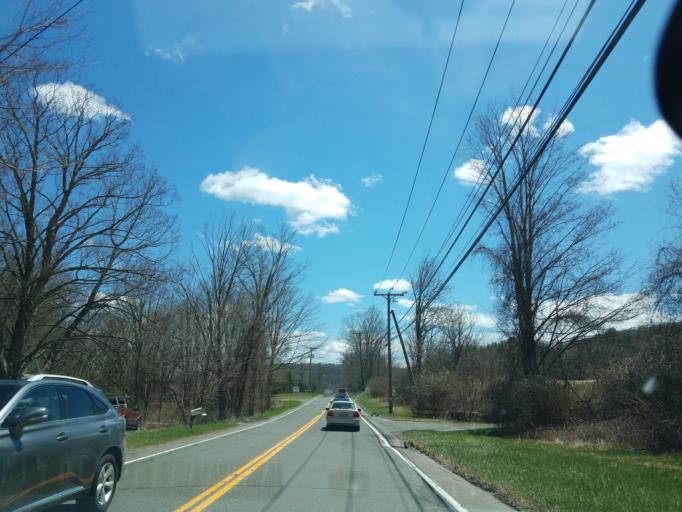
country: US
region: Connecticut
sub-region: Litchfield County
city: New Milford
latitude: 41.5899
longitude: -73.4485
